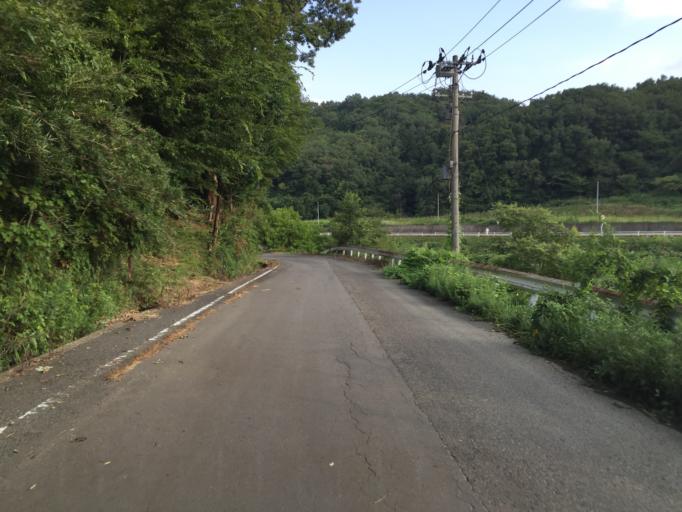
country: JP
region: Fukushima
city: Fukushima-shi
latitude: 37.6830
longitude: 140.5497
